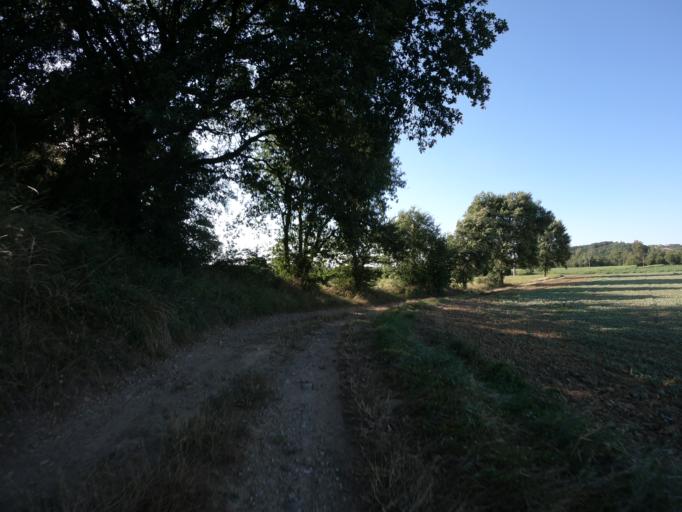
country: FR
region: Midi-Pyrenees
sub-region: Departement de l'Ariege
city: La Tour-du-Crieu
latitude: 43.0965
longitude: 1.7416
